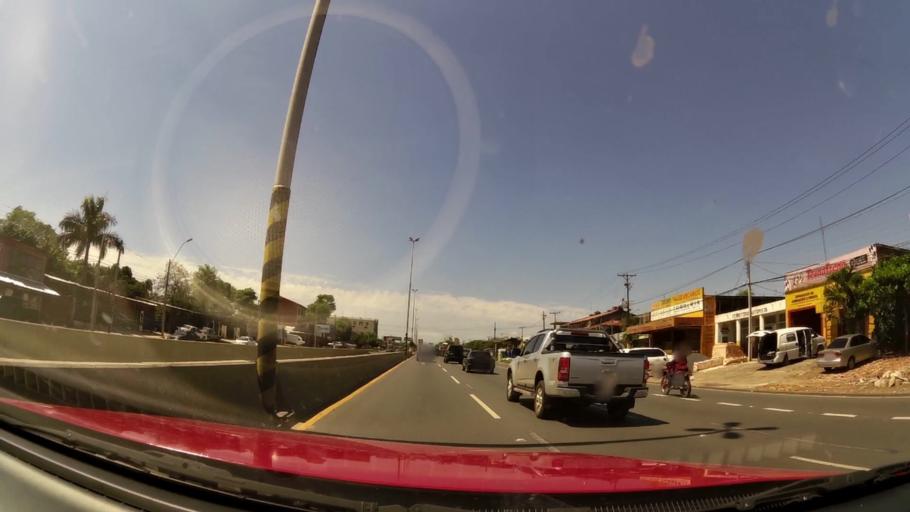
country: PY
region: Central
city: Colonia Mariano Roque Alonso
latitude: -25.2459
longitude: -57.5487
